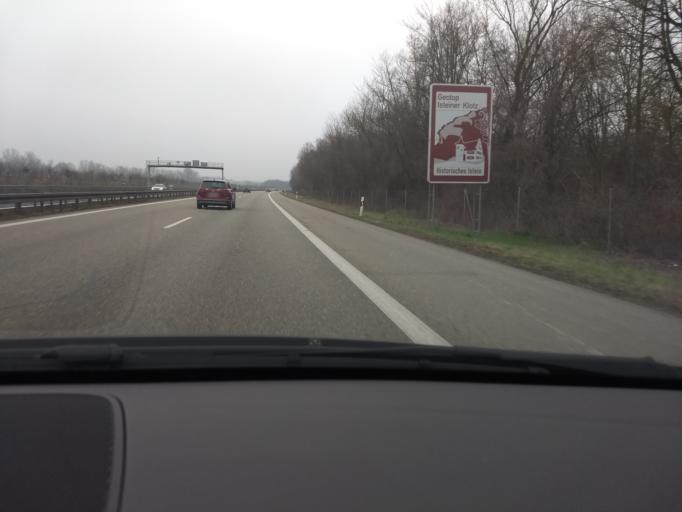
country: FR
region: Alsace
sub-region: Departement du Haut-Rhin
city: Rosenau
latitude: 47.6483
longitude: 7.5441
